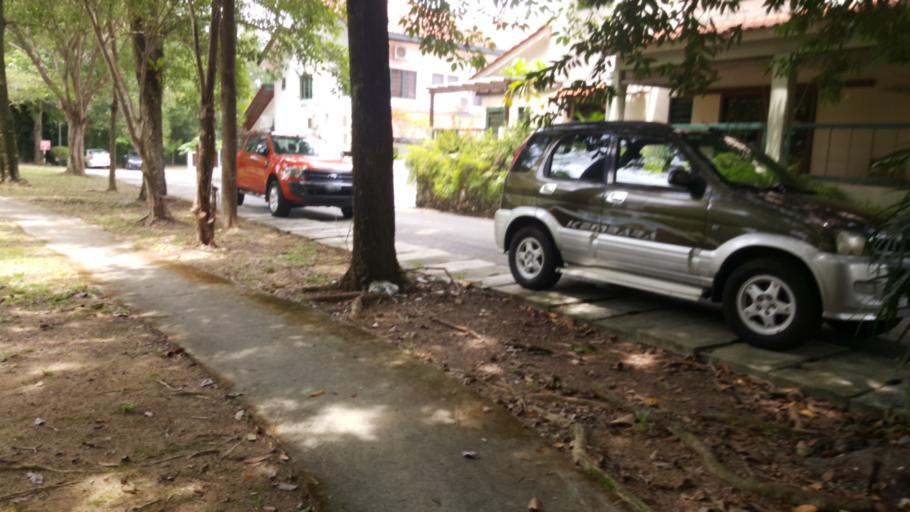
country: MY
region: Selangor
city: Kampung Baru Subang
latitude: 3.1454
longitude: 101.5770
